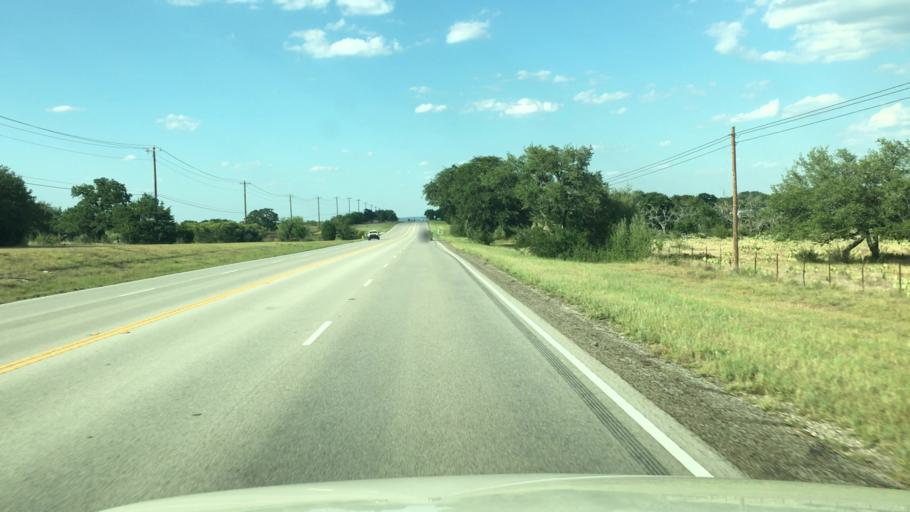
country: US
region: Texas
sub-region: Llano County
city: Horseshoe Bay
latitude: 30.4912
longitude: -98.3103
